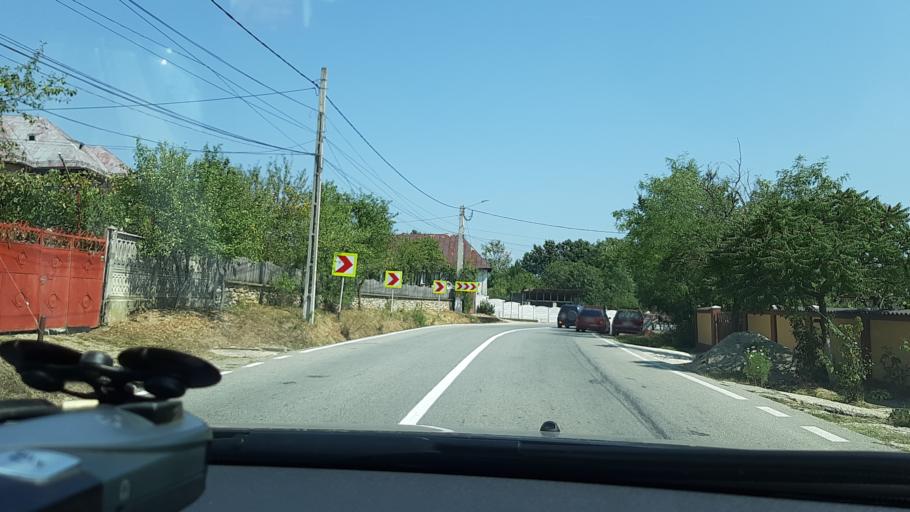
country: RO
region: Gorj
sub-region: Comuna Targu Carbunesti
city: Targu Carbunesti
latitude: 44.9506
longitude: 23.5452
